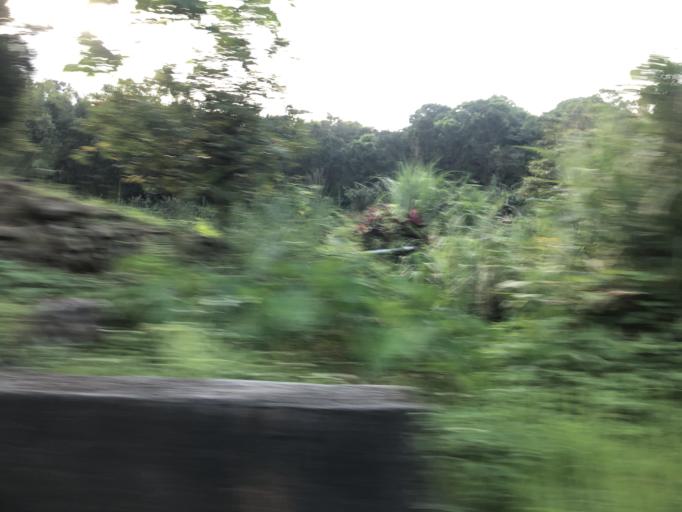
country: TW
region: Taiwan
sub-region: Keelung
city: Keelung
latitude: 25.1964
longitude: 121.6464
